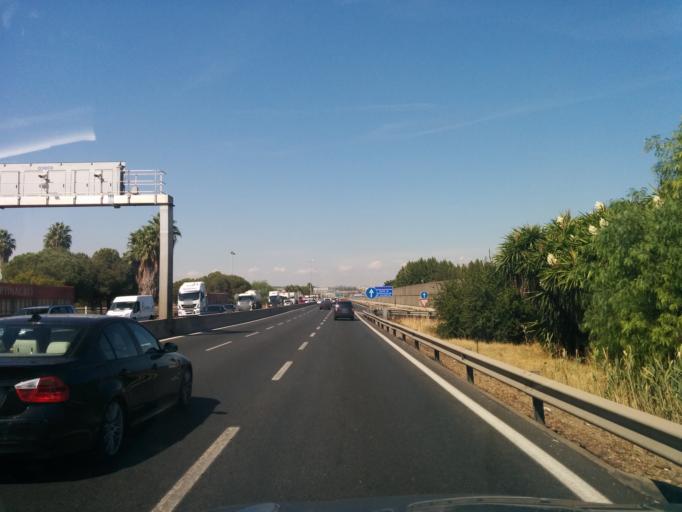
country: ES
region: Andalusia
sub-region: Provincia de Sevilla
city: Gelves
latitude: 37.3589
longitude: -6.0047
